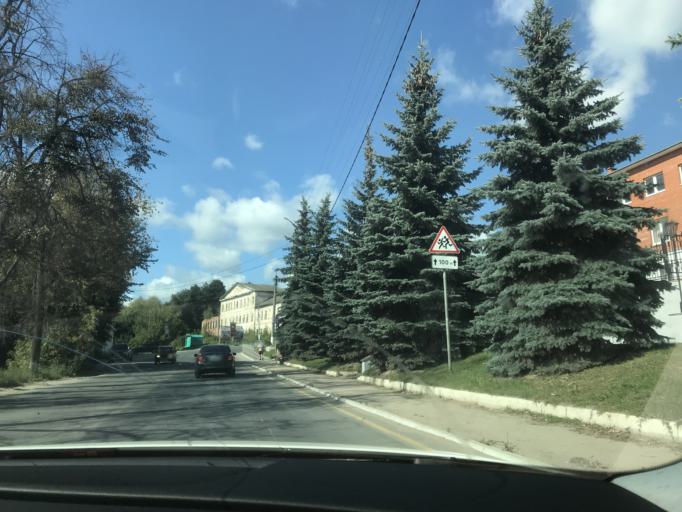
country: RU
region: Kaluga
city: Kondrovo
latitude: 54.8068
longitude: 35.9298
